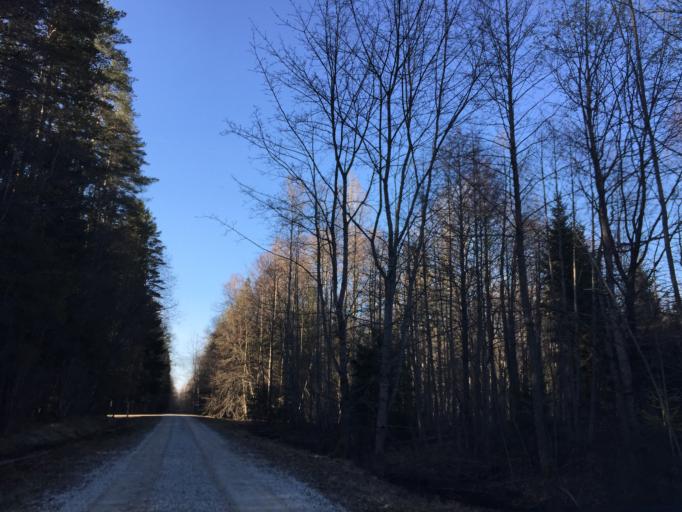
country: EE
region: Ida-Virumaa
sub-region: Sillamaee linn
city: Sillamae
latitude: 59.1688
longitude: 27.7984
